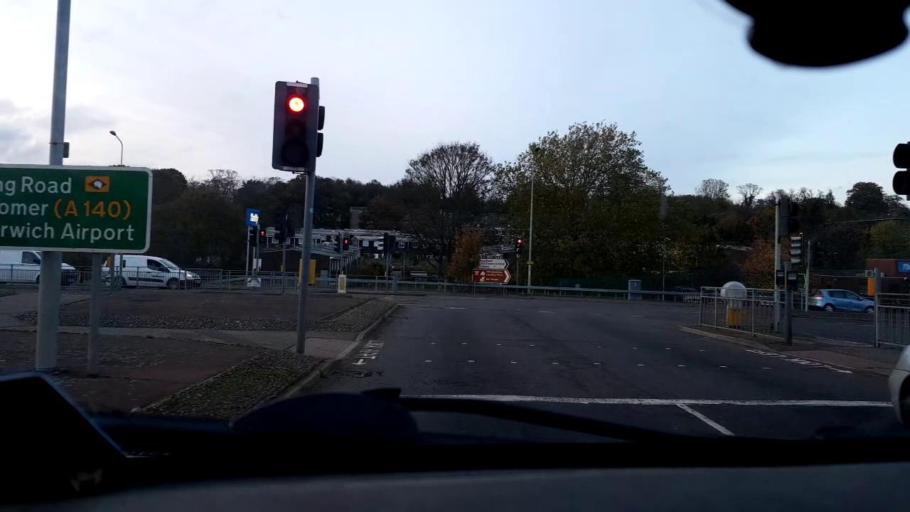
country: GB
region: England
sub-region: Norfolk
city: Thorpe Hamlet
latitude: 52.6117
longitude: 1.3069
